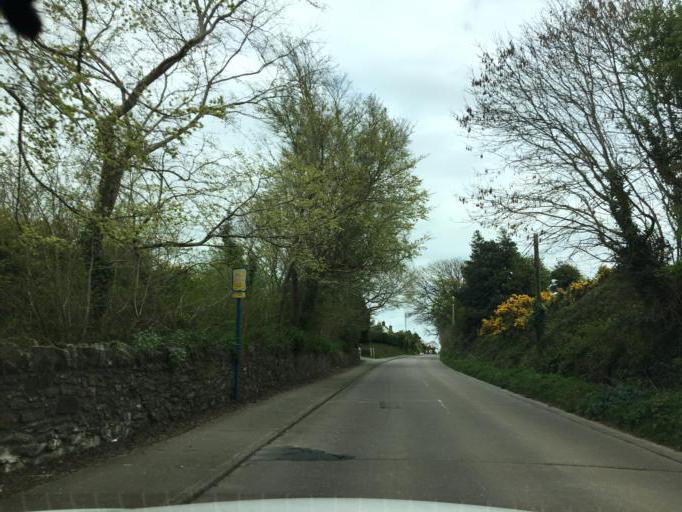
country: IE
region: Leinster
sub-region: Loch Garman
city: Loch Garman
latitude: 52.3504
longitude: -6.5038
